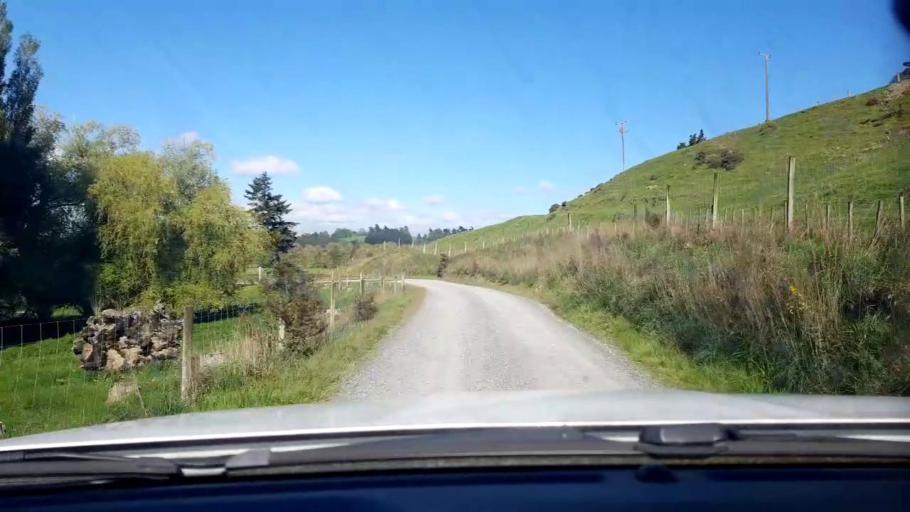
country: NZ
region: Otago
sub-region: Clutha District
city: Balclutha
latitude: -46.2231
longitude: 169.7336
